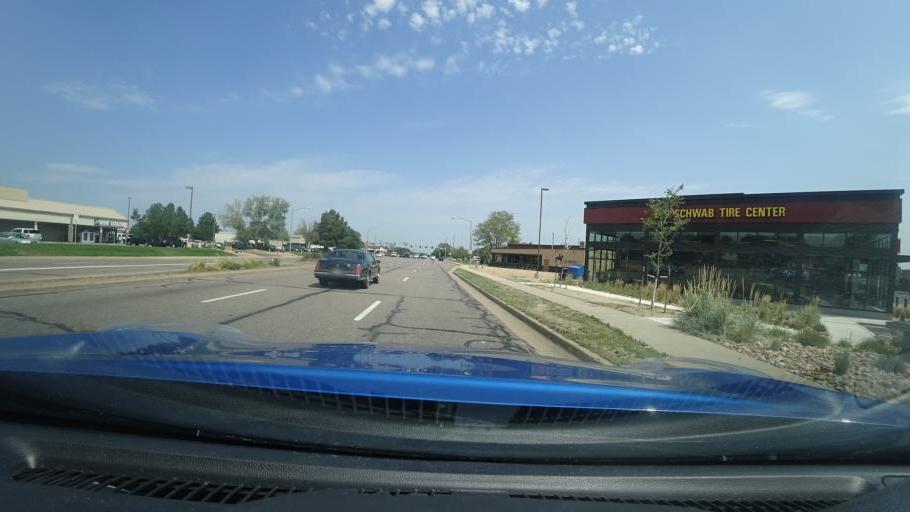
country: US
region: Colorado
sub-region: Adams County
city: Aurora
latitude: 39.6730
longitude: -104.8098
